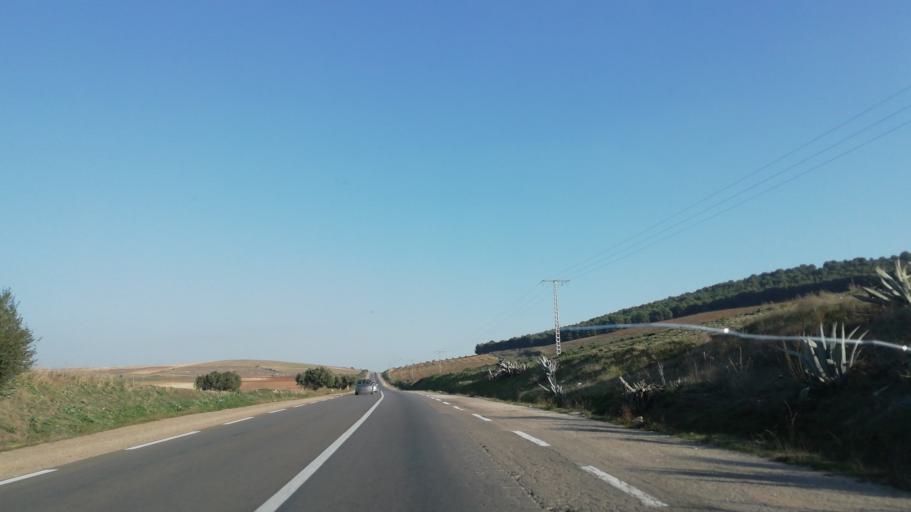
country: DZ
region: Ain Temouchent
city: Hammam Bou Hadjar
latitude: 35.1658
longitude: -0.8863
